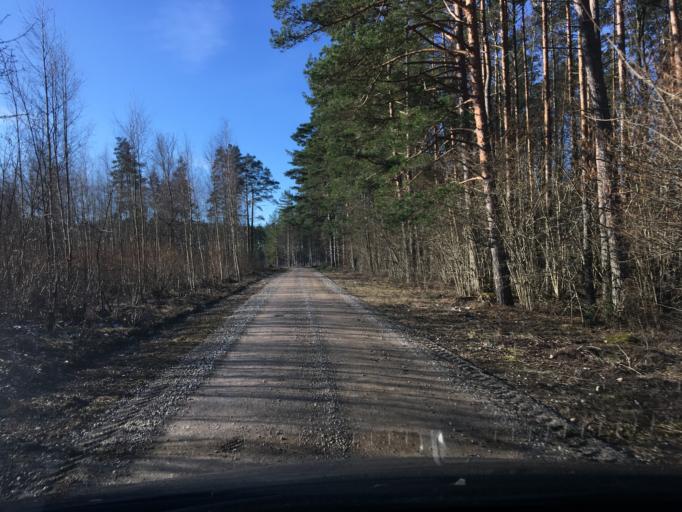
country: EE
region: Laeaene
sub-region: Lihula vald
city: Lihula
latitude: 58.5708
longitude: 23.6935
